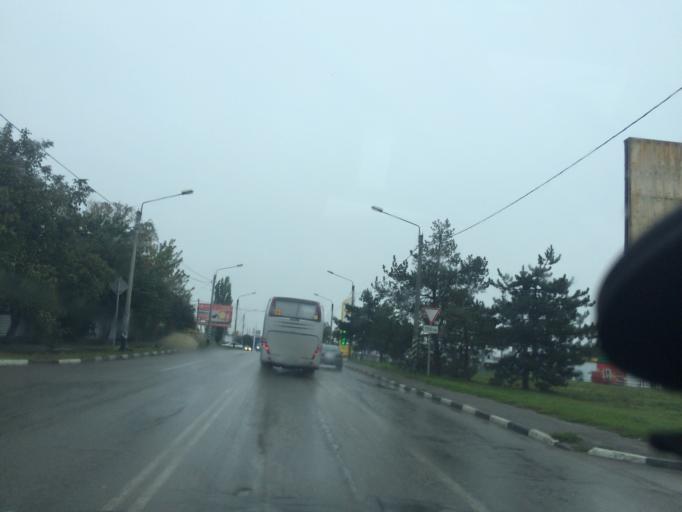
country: RU
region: Rostov
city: Azov
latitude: 47.0913
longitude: 39.4525
